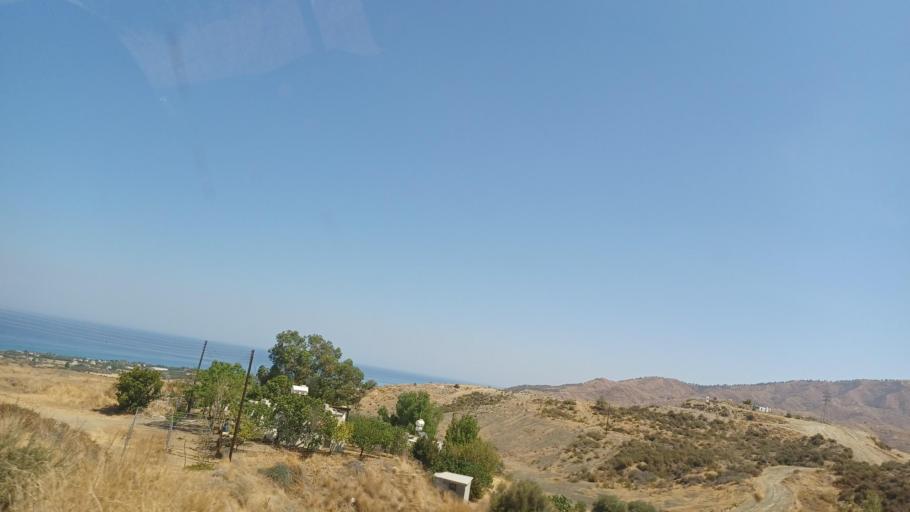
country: CY
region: Pafos
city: Polis
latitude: 35.0468
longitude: 32.4844
